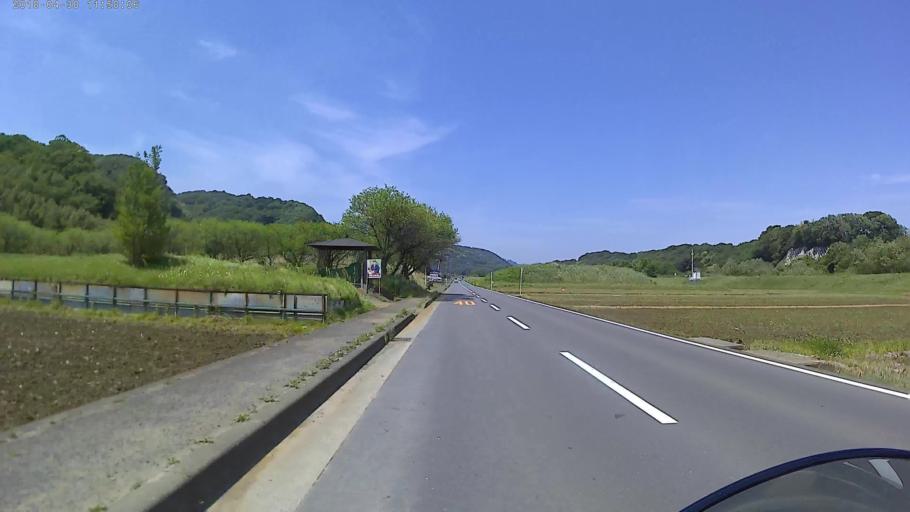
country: JP
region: Kanagawa
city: Zama
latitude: 35.4993
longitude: 139.3385
